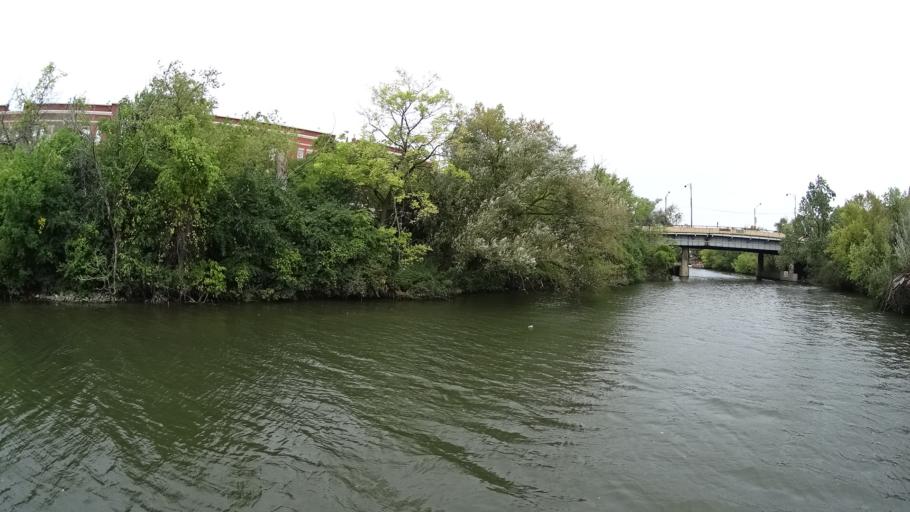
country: US
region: Illinois
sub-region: Cook County
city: Lincolnwood
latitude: 41.9532
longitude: -87.6950
